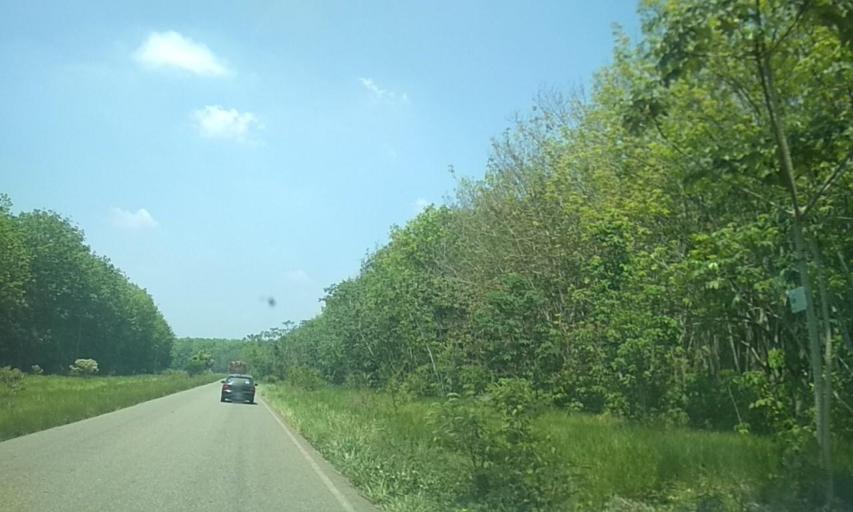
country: MX
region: Tabasco
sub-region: Huimanguillo
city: Paso de la Mina 2da. Seccion (Barrial)
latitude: 17.8114
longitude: -93.6171
